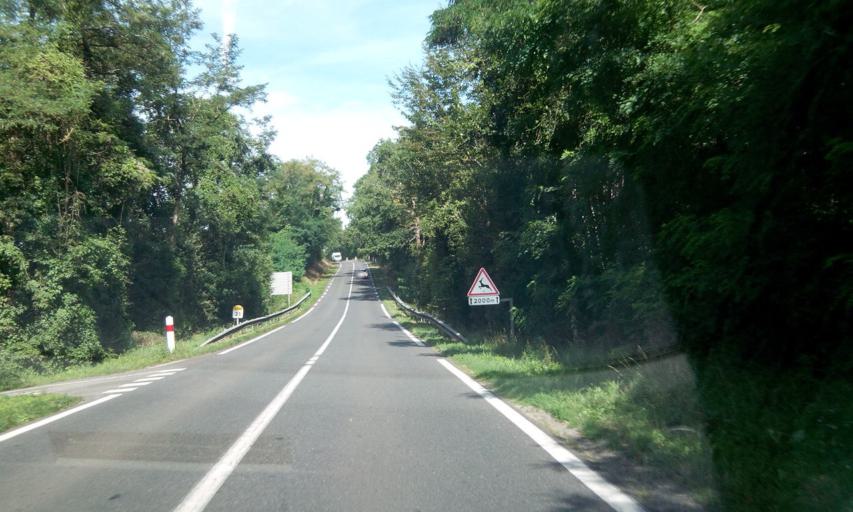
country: FR
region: Poitou-Charentes
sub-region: Departement de la Vienne
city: Charroux
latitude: 46.1537
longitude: 0.3714
